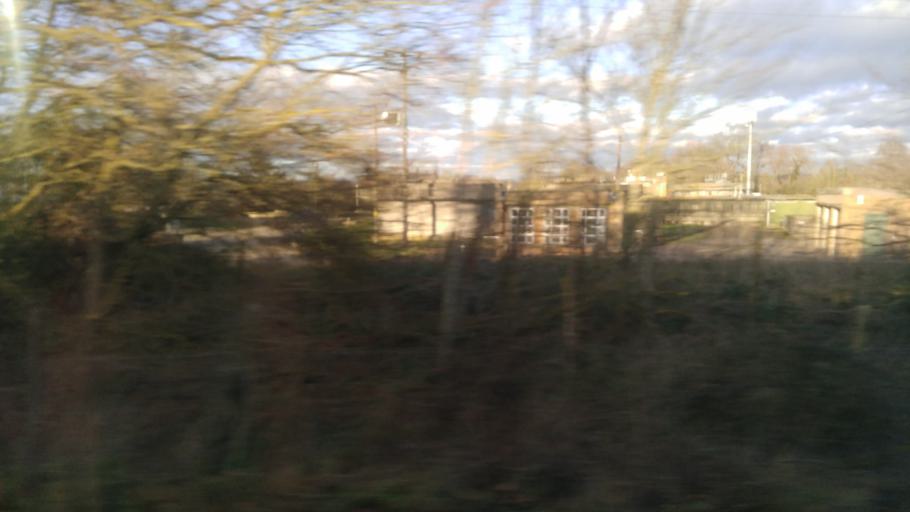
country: GB
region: England
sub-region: Kent
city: Staplehurst
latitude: 51.1711
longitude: 0.5572
